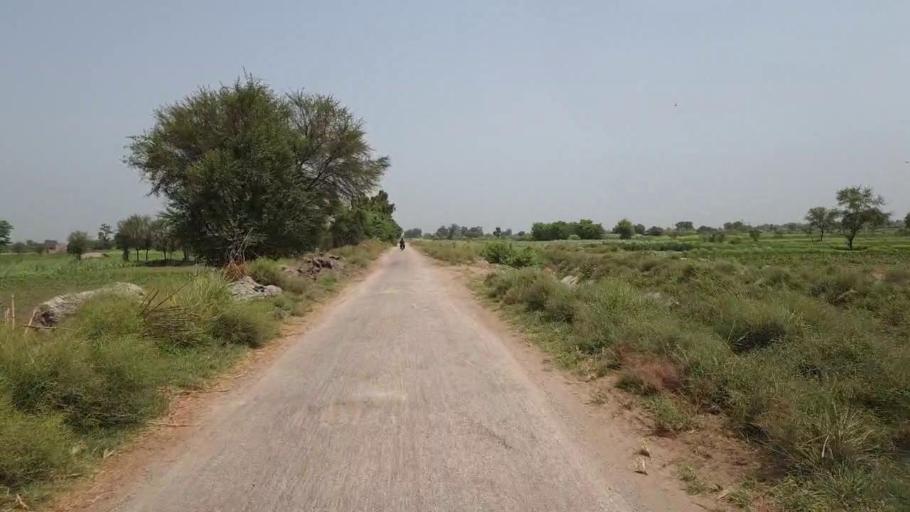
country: PK
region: Sindh
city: Nawabshah
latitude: 26.2754
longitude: 68.3139
